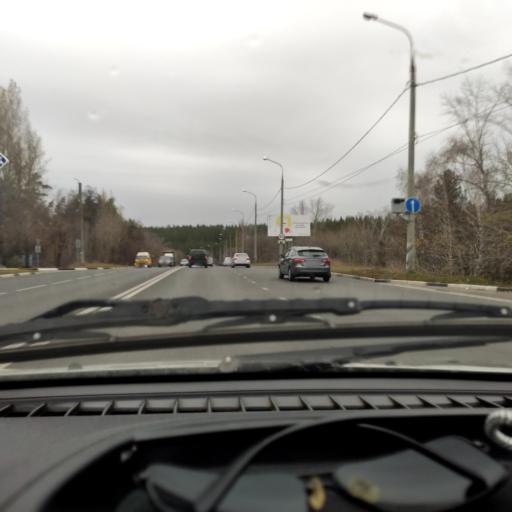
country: RU
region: Samara
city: Zhigulevsk
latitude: 53.4987
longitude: 49.4728
